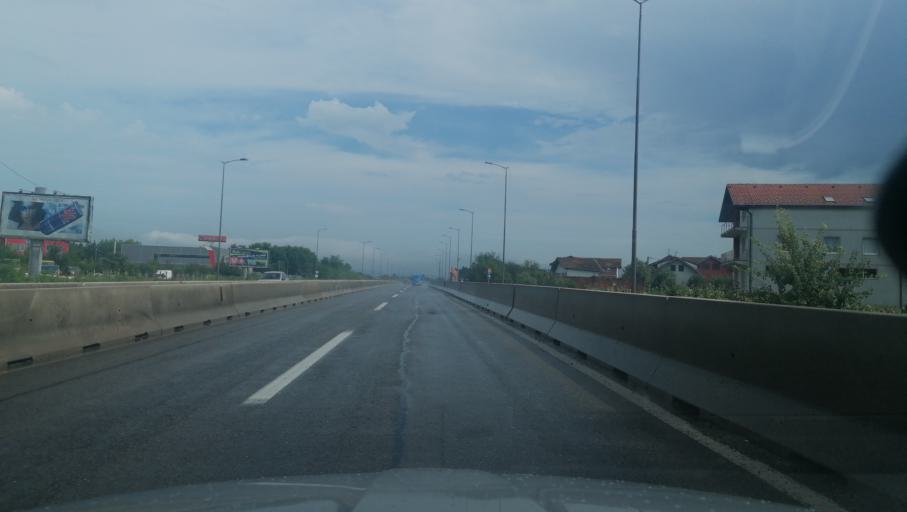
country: BA
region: Republika Srpska
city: Trn
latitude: 44.8254
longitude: 17.2072
